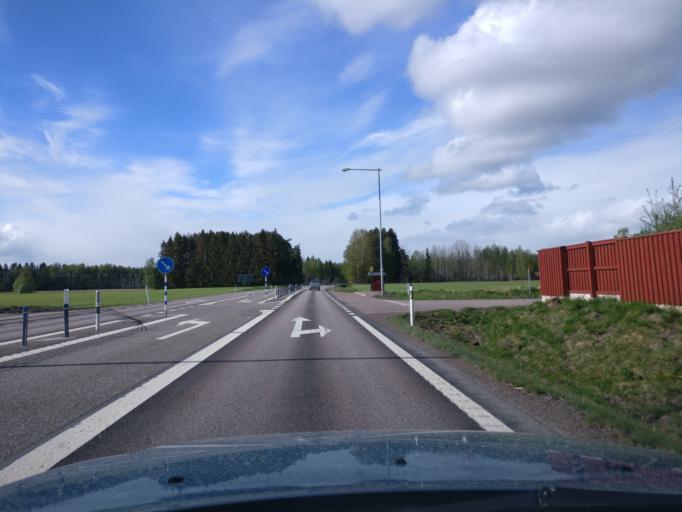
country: SE
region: Vaermland
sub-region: Forshaga Kommun
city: Forshaga
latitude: 59.4700
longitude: 13.4125
